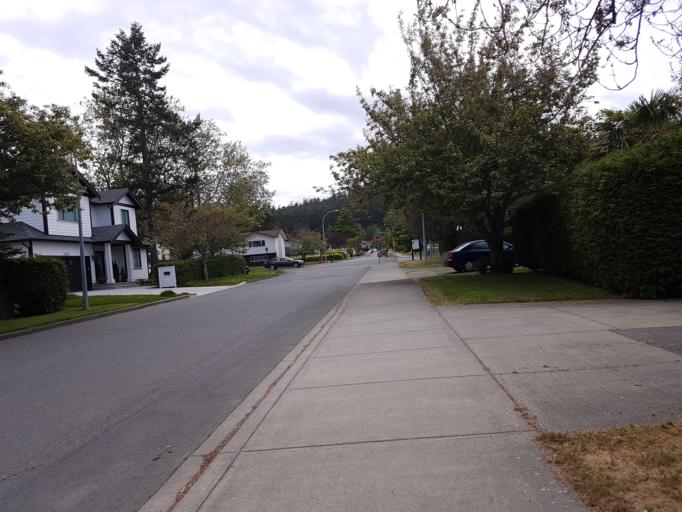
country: CA
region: British Columbia
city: Oak Bay
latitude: 48.4867
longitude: -123.3365
